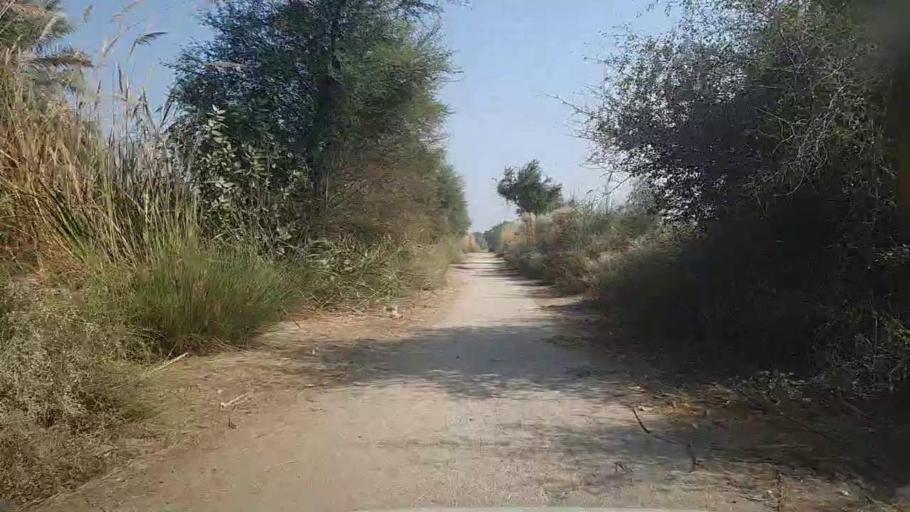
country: PK
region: Sindh
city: Kandiari
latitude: 26.9417
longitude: 68.5352
